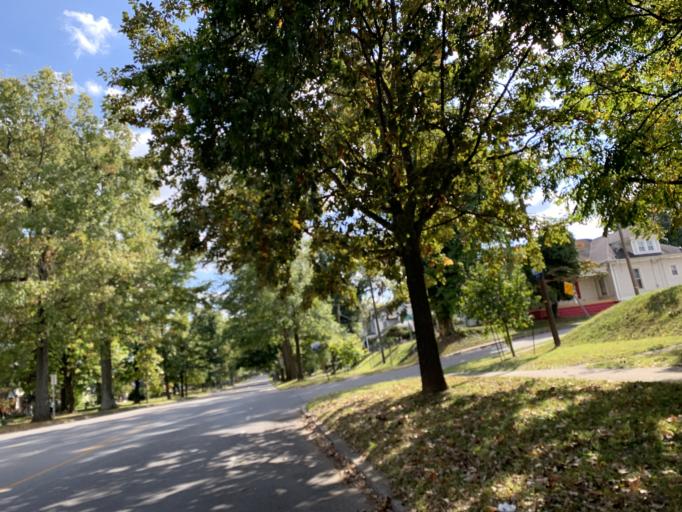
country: US
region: Indiana
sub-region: Floyd County
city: New Albany
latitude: 38.2498
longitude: -85.8295
